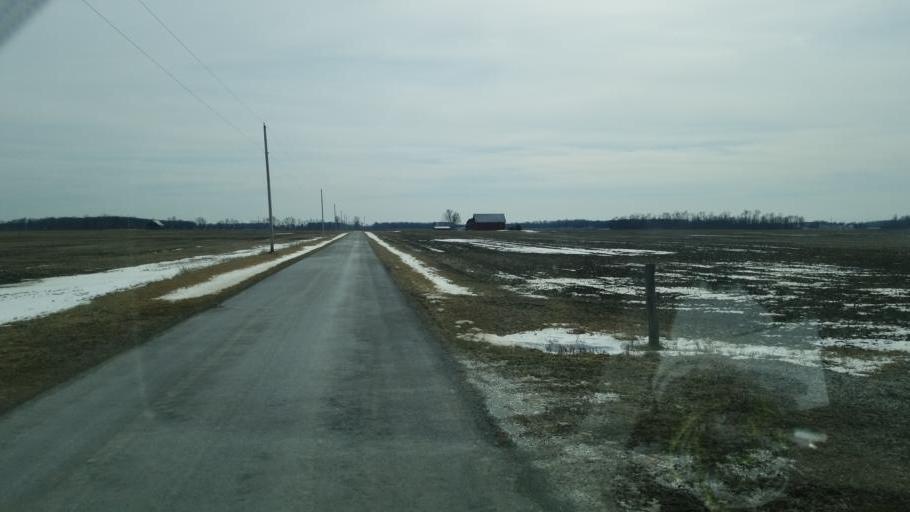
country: US
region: Ohio
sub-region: Delaware County
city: Ashley
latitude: 40.3888
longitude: -82.9952
